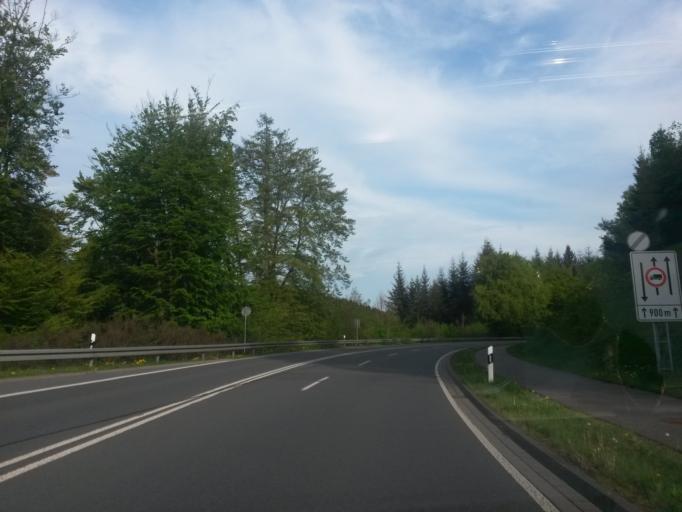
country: DE
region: North Rhine-Westphalia
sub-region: Regierungsbezirk Arnsberg
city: Herscheid
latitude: 51.1937
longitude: 7.6907
